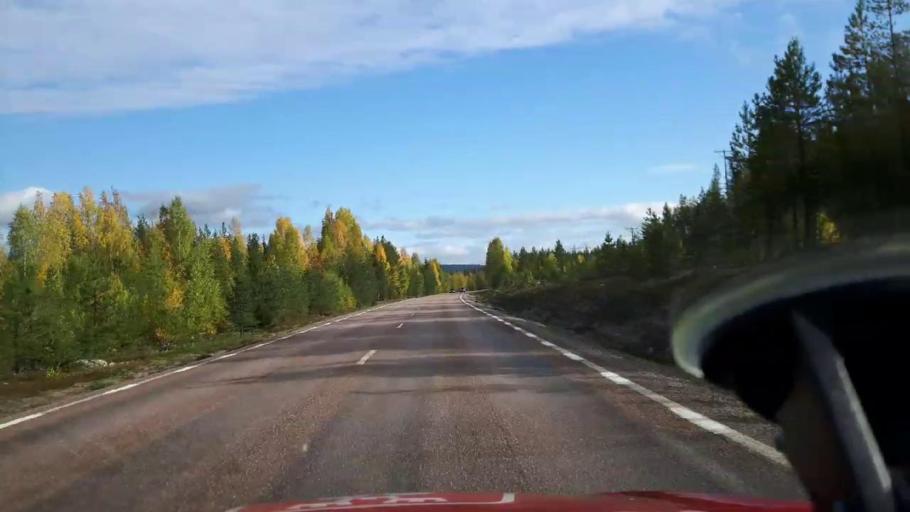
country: SE
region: Gaevleborg
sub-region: Ljusdals Kommun
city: Farila
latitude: 61.9405
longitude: 15.4299
